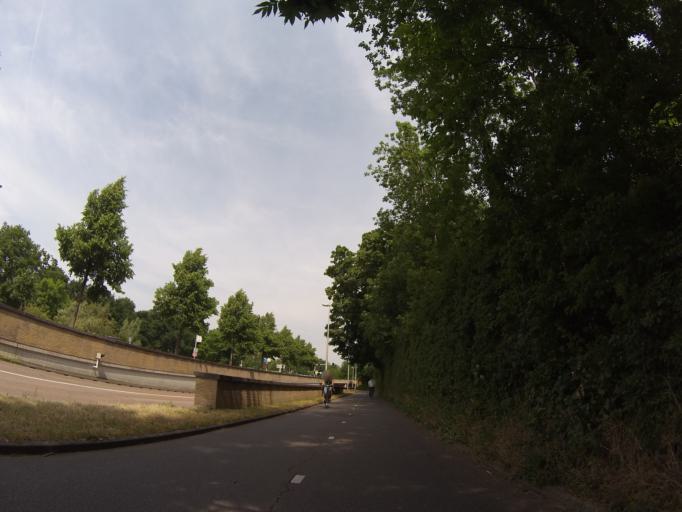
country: NL
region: Utrecht
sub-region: Gemeente Utrecht
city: Utrecht
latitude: 52.0948
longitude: 5.1449
